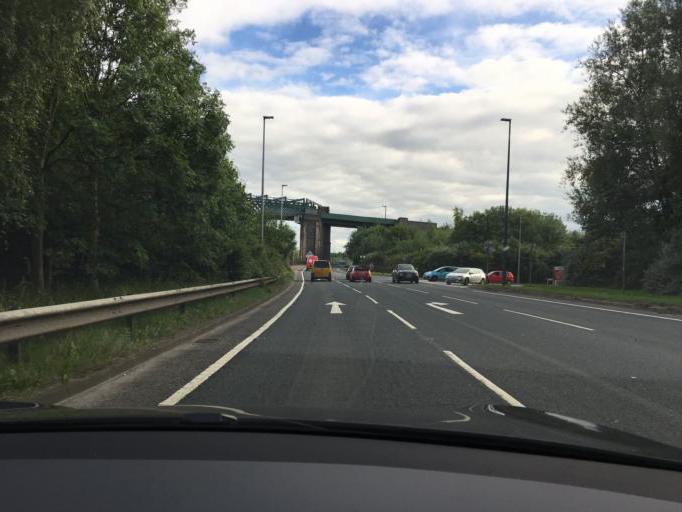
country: GB
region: England
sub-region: City and Borough of Salford
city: Irlam
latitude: 53.4408
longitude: -2.4132
